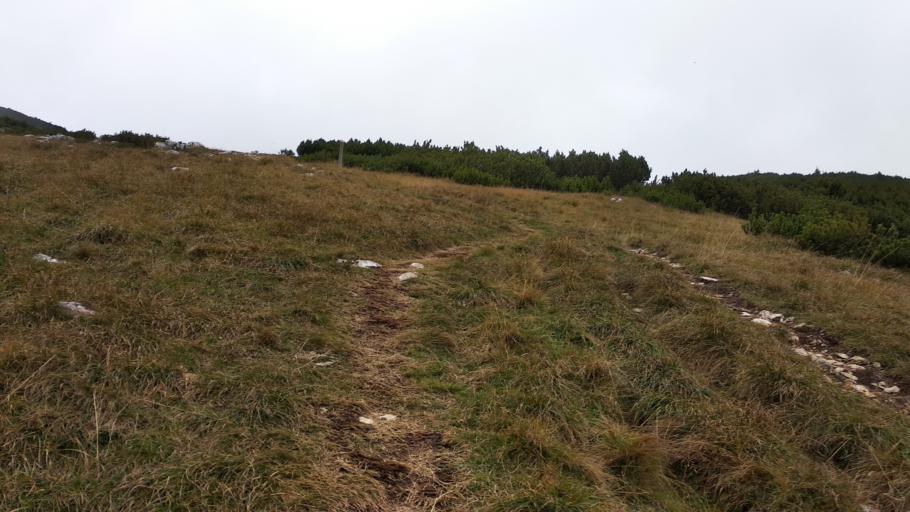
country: IT
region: Veneto
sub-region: Provincia di Vicenza
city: Roana
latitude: 45.9615
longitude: 11.4537
